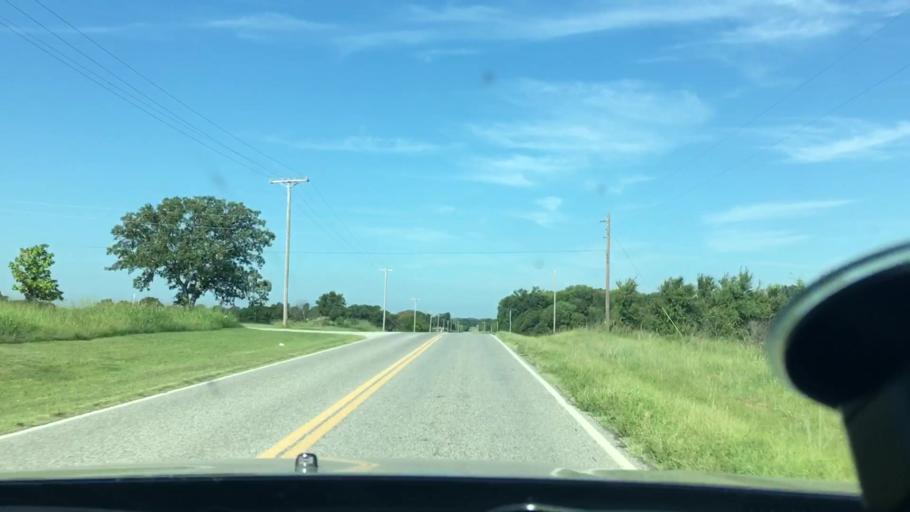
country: US
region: Oklahoma
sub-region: Johnston County
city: Tishomingo
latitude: 34.2733
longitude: -96.4321
